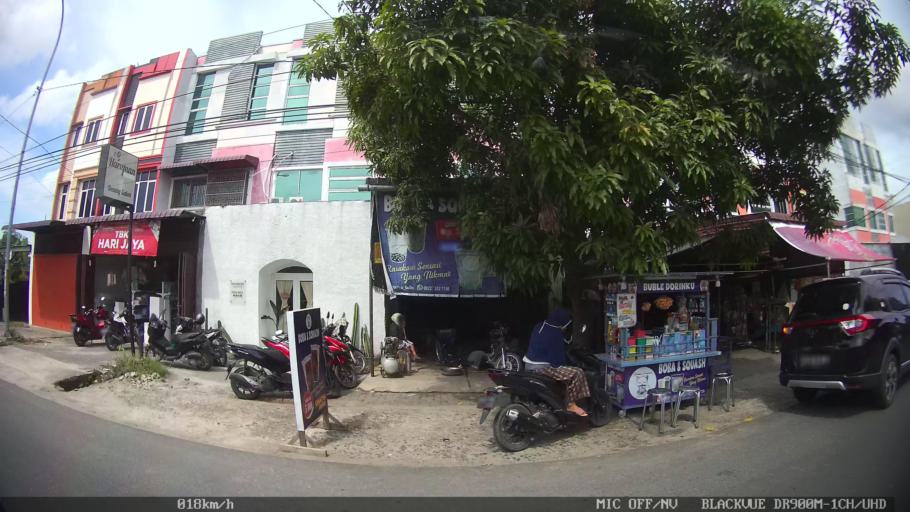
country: ID
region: North Sumatra
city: Percut
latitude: 3.5730
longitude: 98.8689
